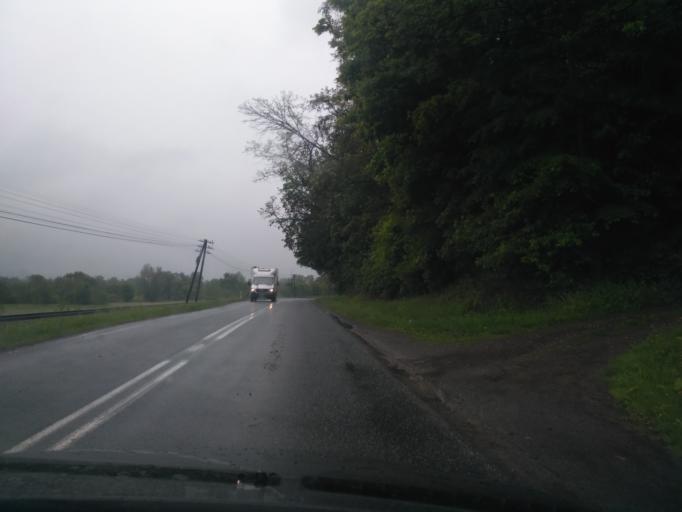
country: PL
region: Subcarpathian Voivodeship
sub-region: Powiat krosnienski
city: Leki
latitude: 49.8100
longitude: 21.6369
